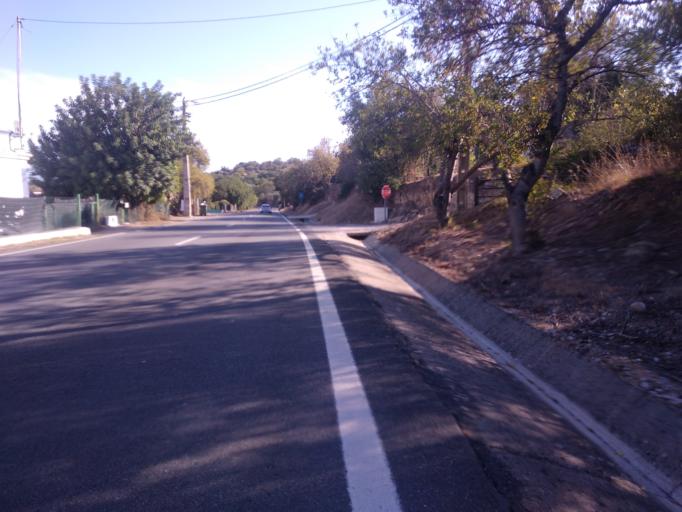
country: PT
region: Faro
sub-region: Sao Bras de Alportel
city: Sao Bras de Alportel
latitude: 37.1107
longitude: -7.9083
